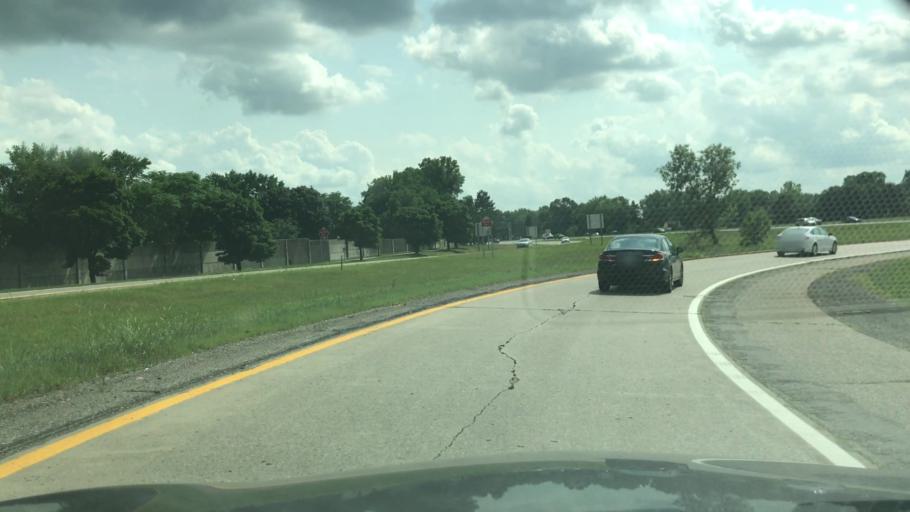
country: US
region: Michigan
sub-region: Wayne County
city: Plymouth
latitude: 42.3587
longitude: -83.4341
